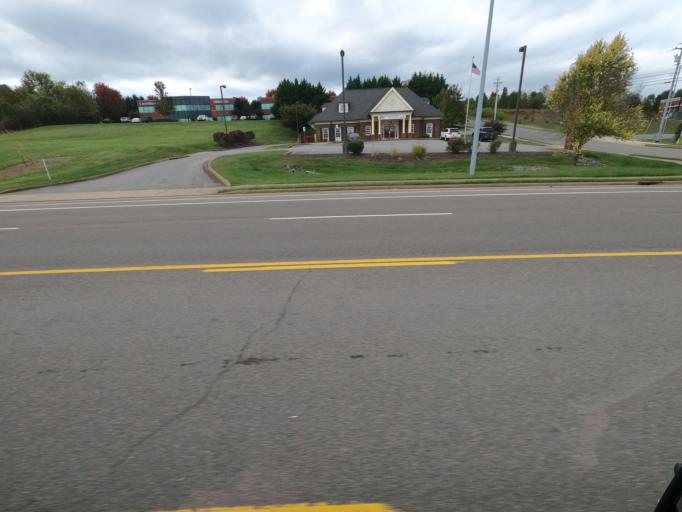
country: US
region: Tennessee
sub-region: Washington County
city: Oak Grove
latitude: 36.3825
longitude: -82.4226
